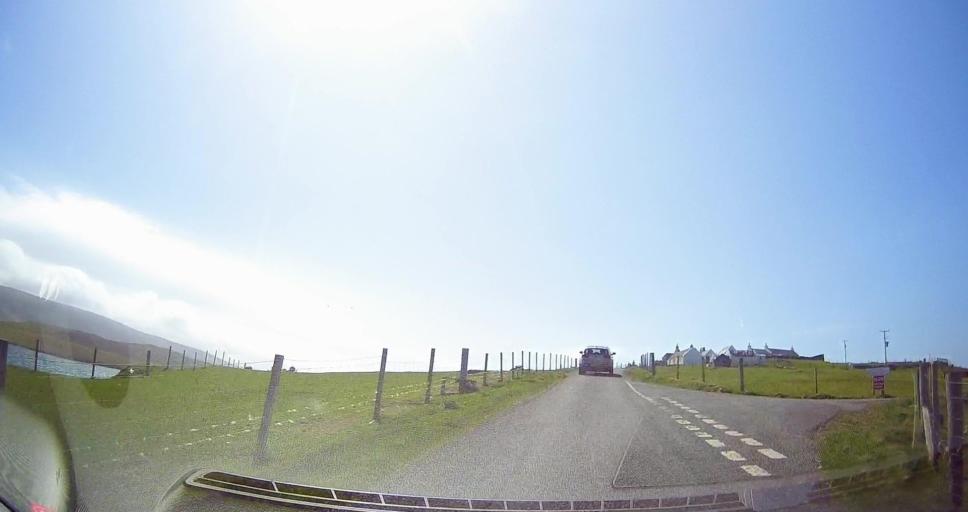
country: GB
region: Scotland
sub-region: Shetland Islands
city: Sandwick
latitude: 60.0638
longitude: -1.3400
